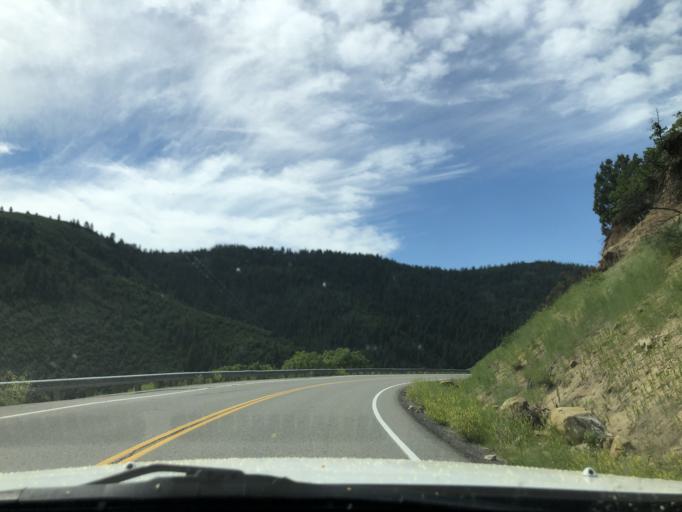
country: US
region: Colorado
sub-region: Delta County
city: Paonia
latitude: 38.9553
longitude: -107.3434
